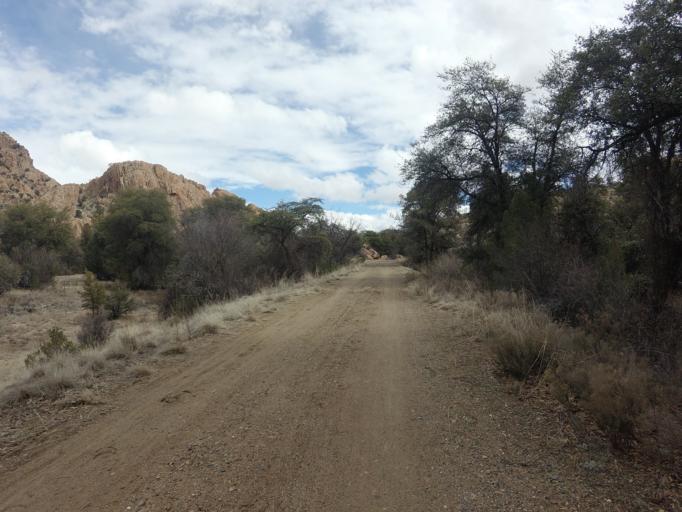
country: US
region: Arizona
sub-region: Yavapai County
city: Prescott Valley
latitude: 34.6072
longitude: -112.3987
